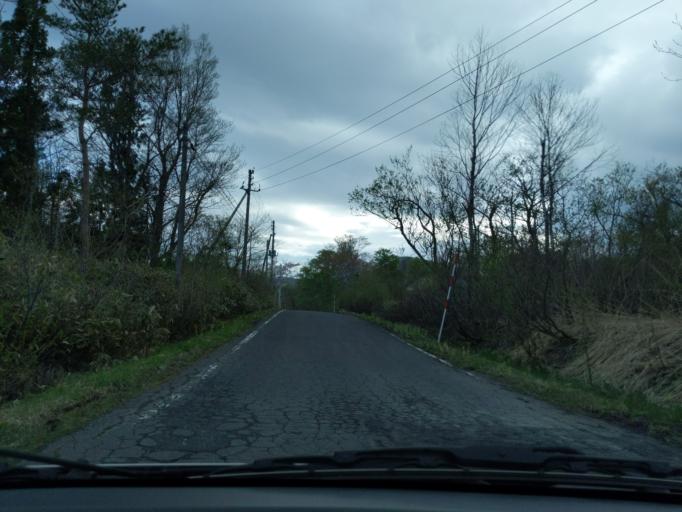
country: JP
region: Iwate
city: Ichinoseki
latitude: 38.9265
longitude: 140.8279
